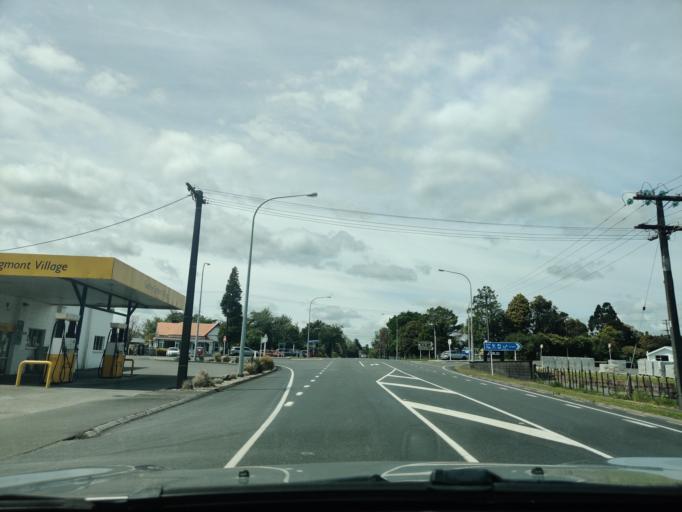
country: NZ
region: Taranaki
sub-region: New Plymouth District
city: New Plymouth
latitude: -39.1452
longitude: 174.1444
